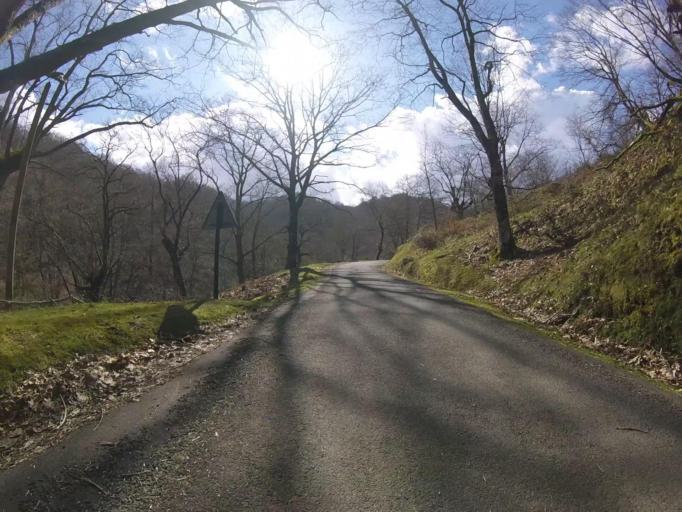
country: ES
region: Navarre
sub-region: Provincia de Navarra
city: Etxalar
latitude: 43.2632
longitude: -1.6058
